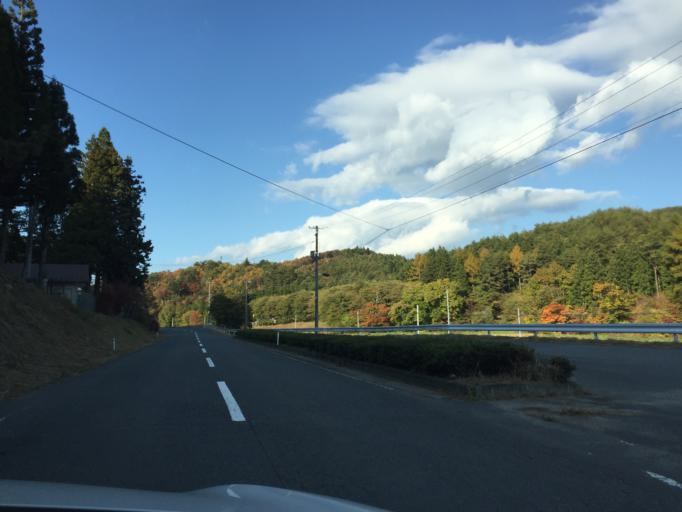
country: JP
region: Fukushima
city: Iwaki
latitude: 37.2665
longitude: 140.7647
